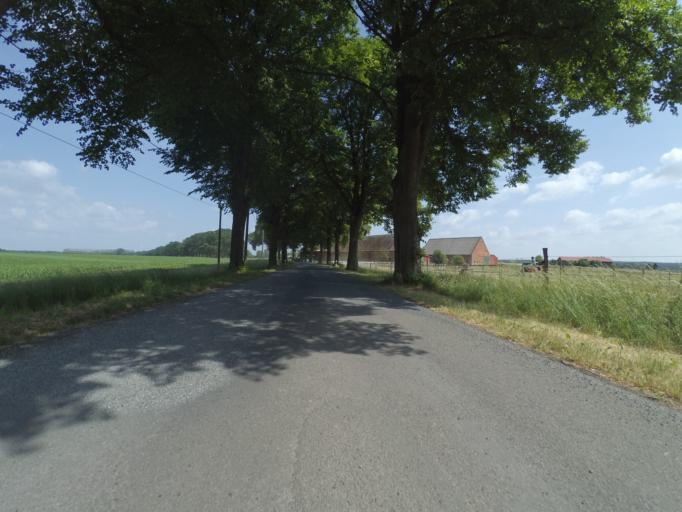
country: DE
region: Mecklenburg-Vorpommern
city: Lubz
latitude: 53.4403
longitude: 12.0911
